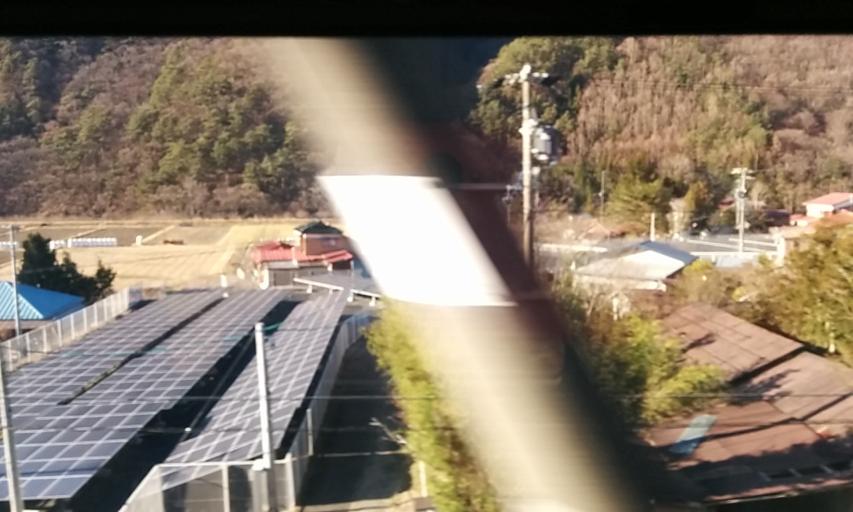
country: JP
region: Nagano
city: Ina
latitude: 35.8828
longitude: 137.7573
